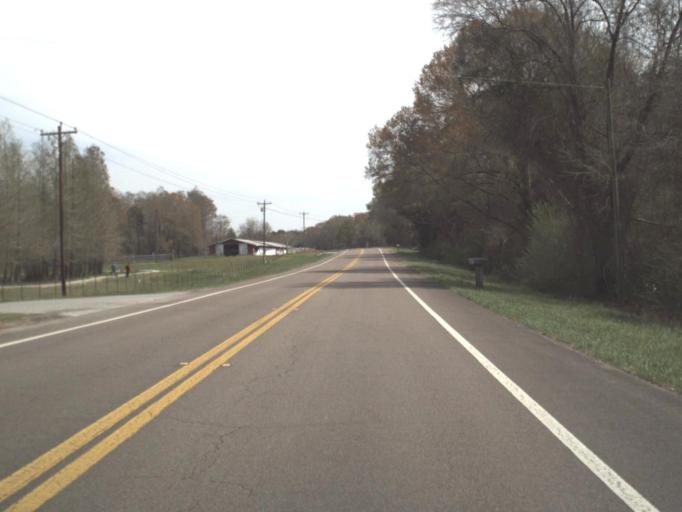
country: US
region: Alabama
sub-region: Geneva County
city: Hartford
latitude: 30.9605
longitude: -85.6970
